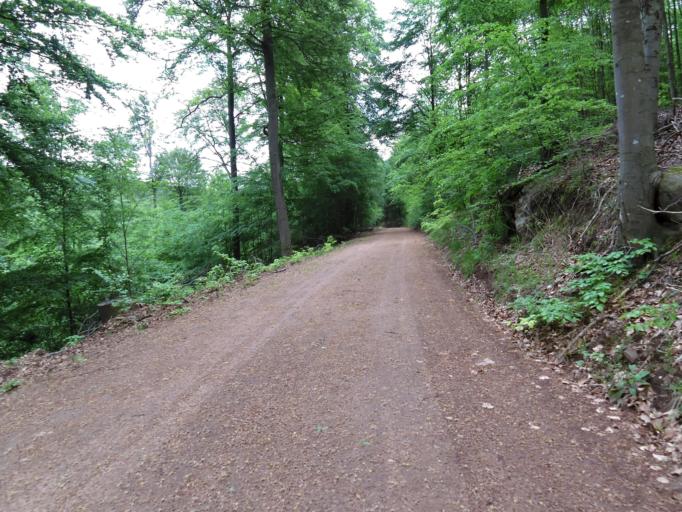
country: DE
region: Rheinland-Pfalz
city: Neidenfels
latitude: 49.4166
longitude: 8.0448
